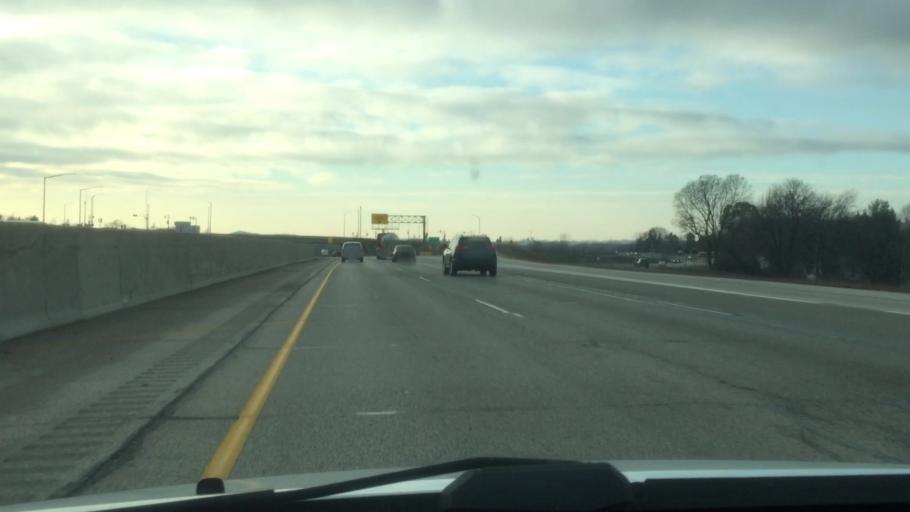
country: US
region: Wisconsin
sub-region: Waukesha County
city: Pewaukee
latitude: 43.0506
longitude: -88.2991
